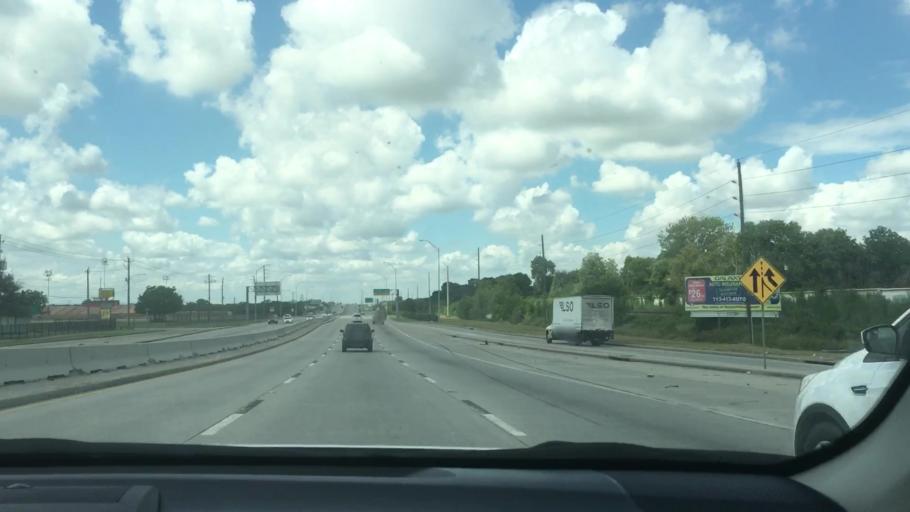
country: US
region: Texas
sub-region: Fort Bend County
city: Missouri City
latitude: 29.6396
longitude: -95.4840
